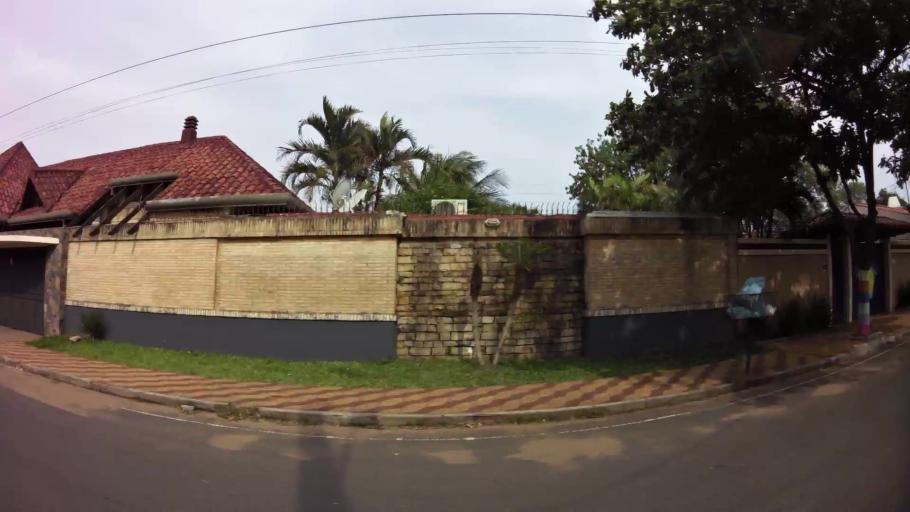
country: PY
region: Central
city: Fernando de la Mora
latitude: -25.2973
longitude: -57.5581
